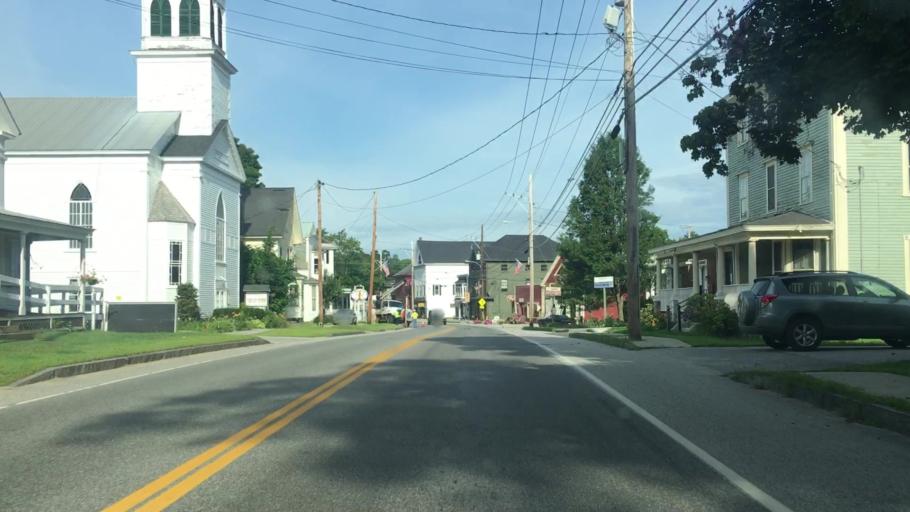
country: US
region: Maine
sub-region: York County
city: Cornish
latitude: 43.8048
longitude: -70.8002
